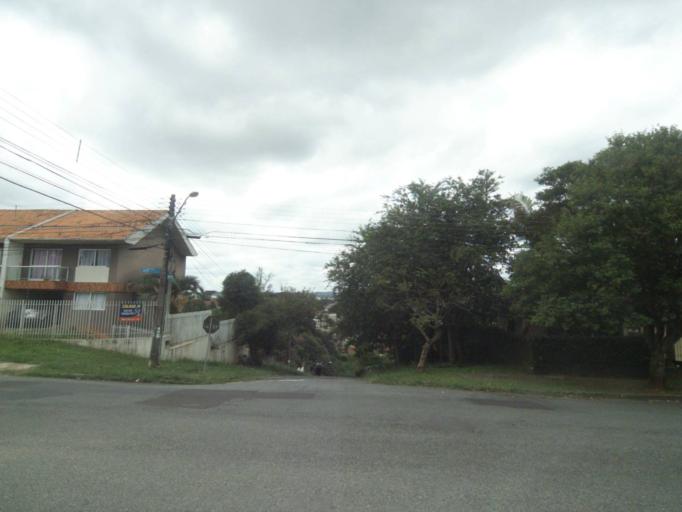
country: BR
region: Parana
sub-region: Curitiba
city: Curitiba
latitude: -25.3923
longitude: -49.2847
